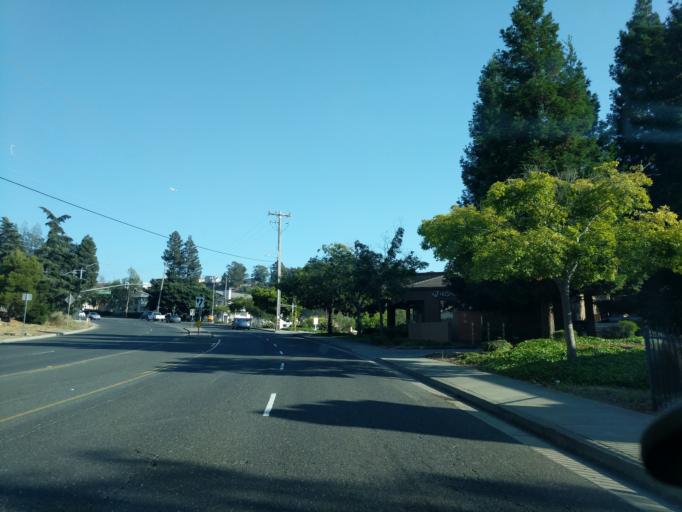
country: US
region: California
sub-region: Alameda County
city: Fairview
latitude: 37.6563
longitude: -122.0489
